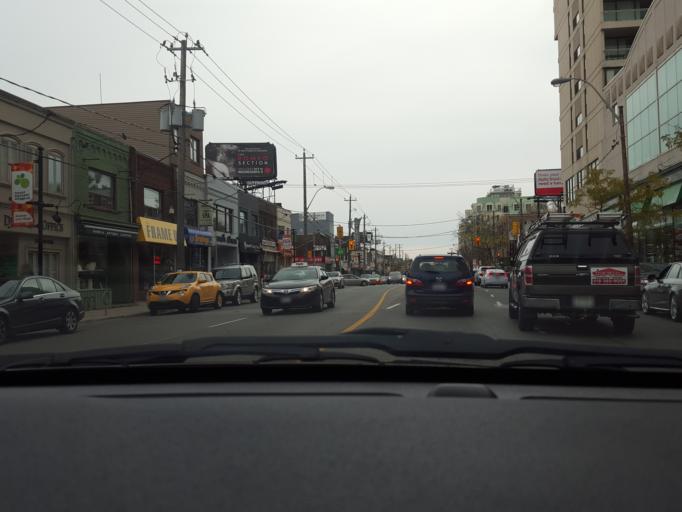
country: CA
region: Ontario
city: Toronto
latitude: 43.7067
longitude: -79.3895
